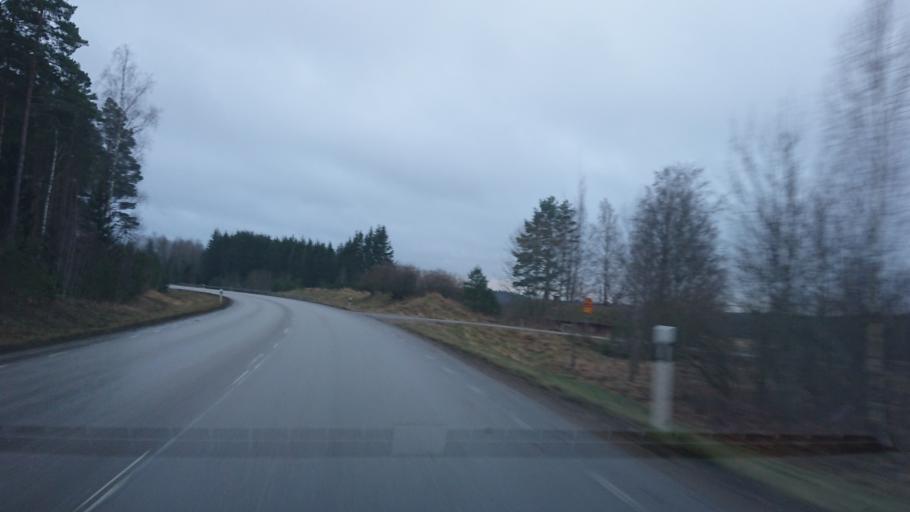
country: SE
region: Uppsala
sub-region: Osthammars Kommun
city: Bjorklinge
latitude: 60.0132
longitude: 17.5871
